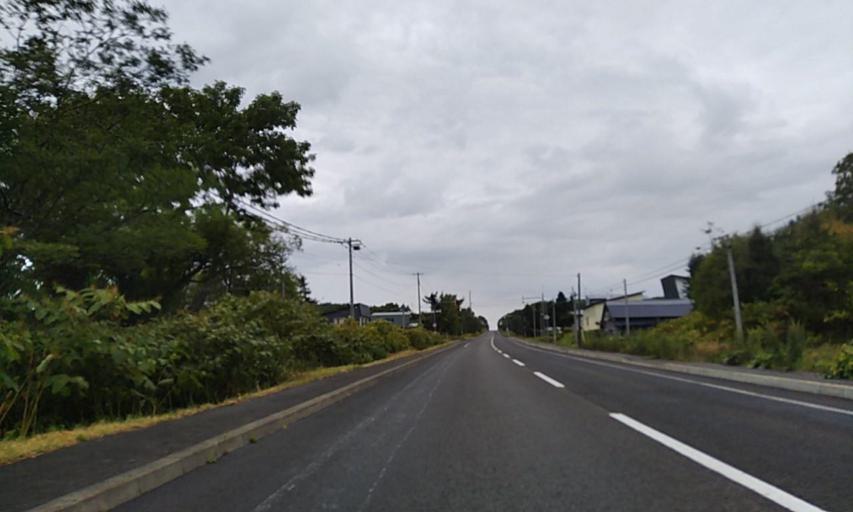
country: JP
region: Hokkaido
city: Mombetsu
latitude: 44.5270
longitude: 143.0462
